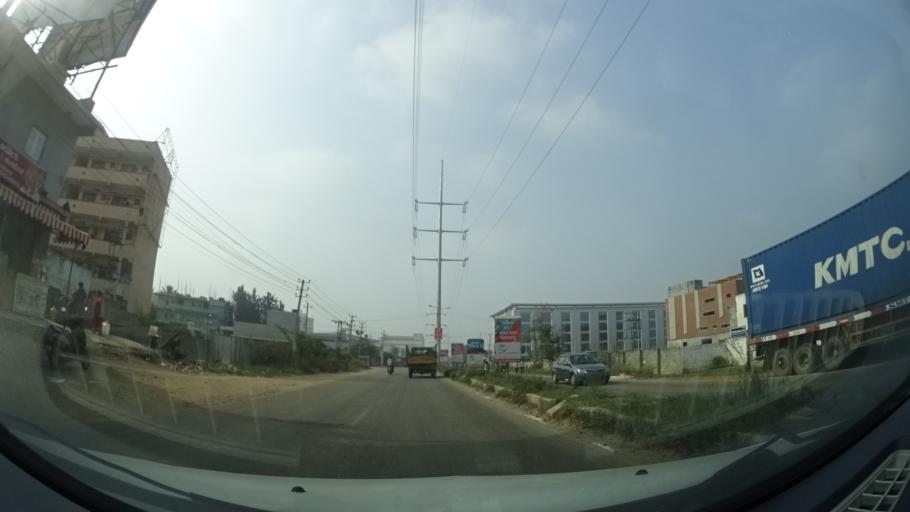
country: IN
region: Karnataka
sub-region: Bangalore Urban
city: Anekal
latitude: 12.7921
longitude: 77.6581
